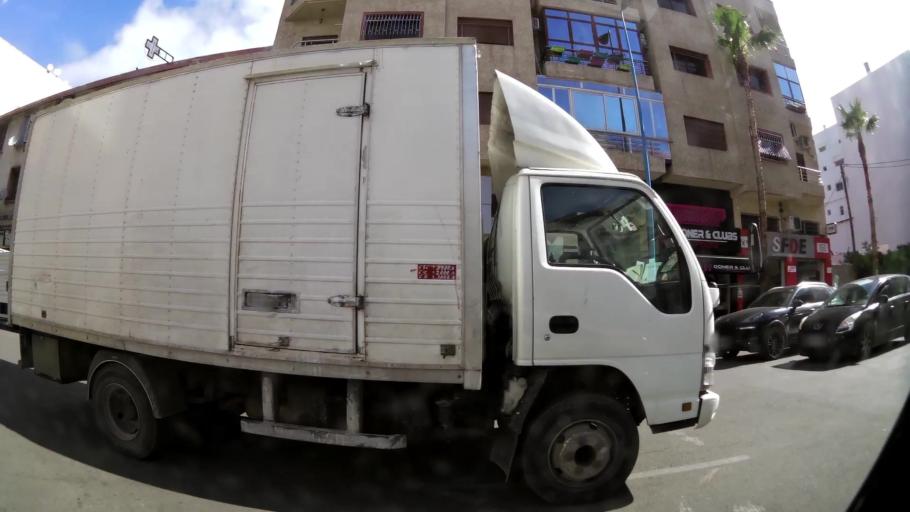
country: MA
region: Grand Casablanca
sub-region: Casablanca
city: Casablanca
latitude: 33.5962
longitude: -7.5888
